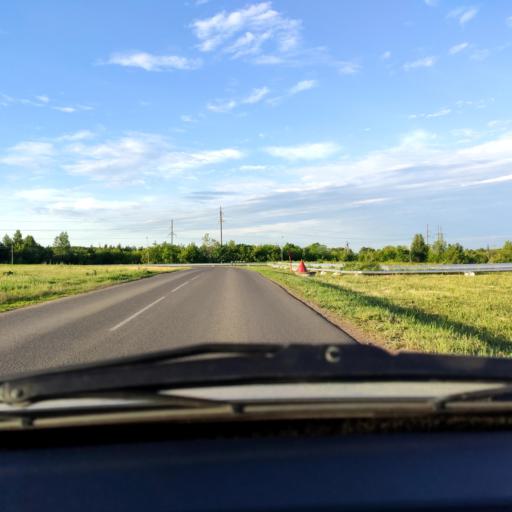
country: RU
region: Bashkortostan
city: Blagoveshchensk
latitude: 54.9105
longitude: 56.0538
